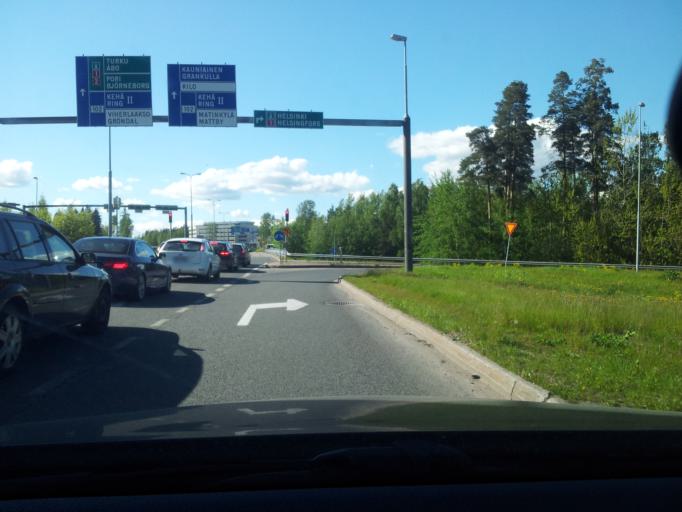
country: FI
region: Uusimaa
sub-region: Helsinki
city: Kilo
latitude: 60.2052
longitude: 24.7579
